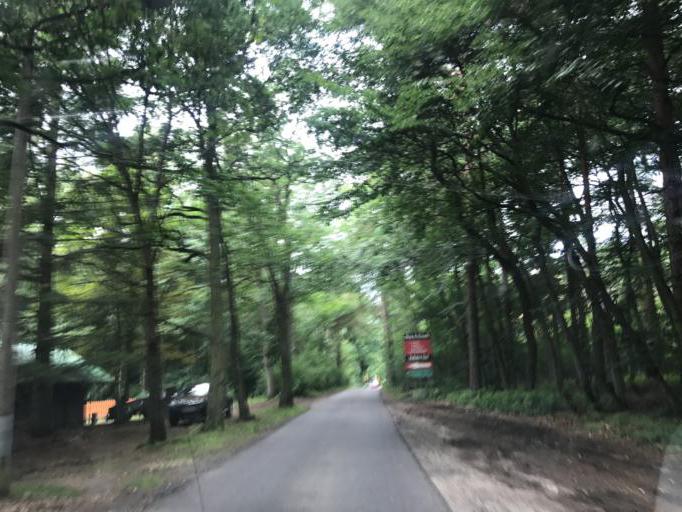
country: DE
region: Brandenburg
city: Rheinsberg
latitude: 53.1562
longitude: 12.8798
